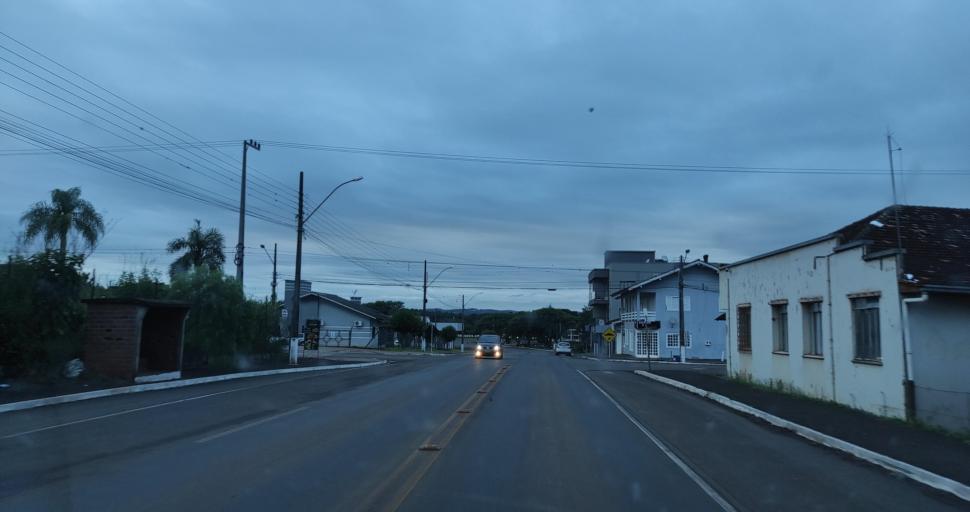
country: BR
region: Santa Catarina
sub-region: Xanxere
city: Xanxere
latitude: -26.7331
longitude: -52.3921
